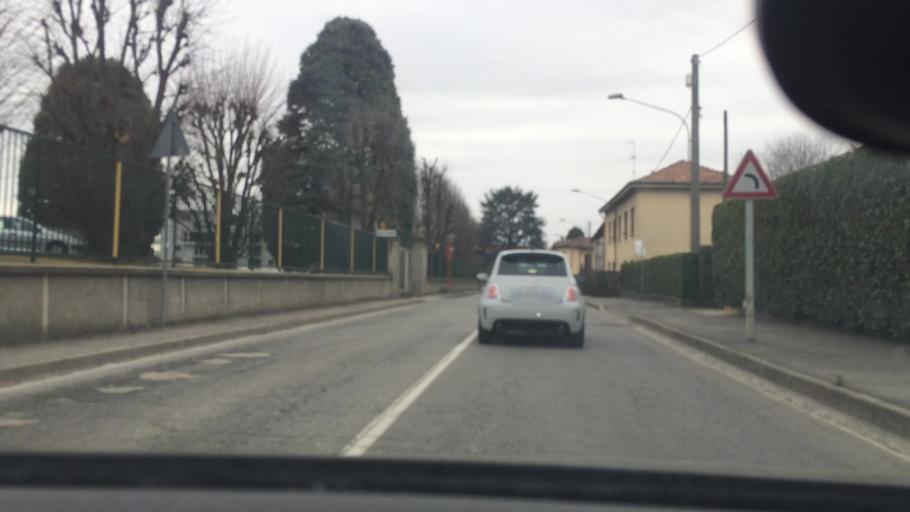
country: IT
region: Lombardy
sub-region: Provincia di Como
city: Arosio
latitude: 45.7185
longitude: 9.2042
